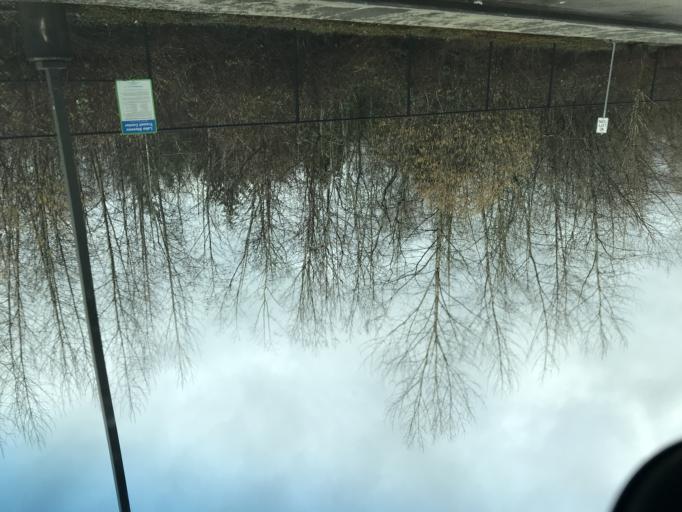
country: US
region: Washington
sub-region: Snohomish County
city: West Lake Stevens
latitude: 47.9978
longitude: -122.1038
